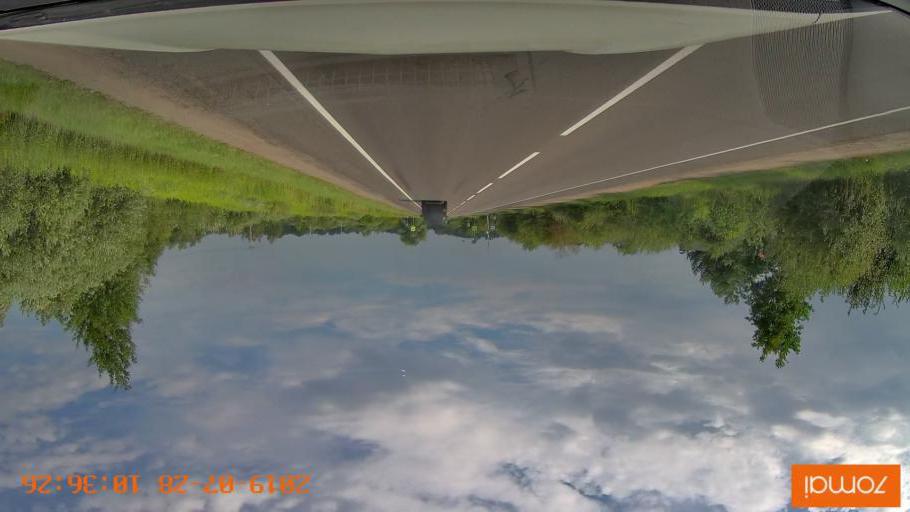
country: RU
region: Kaliningrad
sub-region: Gorod Kaliningrad
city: Kaliningrad
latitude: 54.7381
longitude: 20.4213
